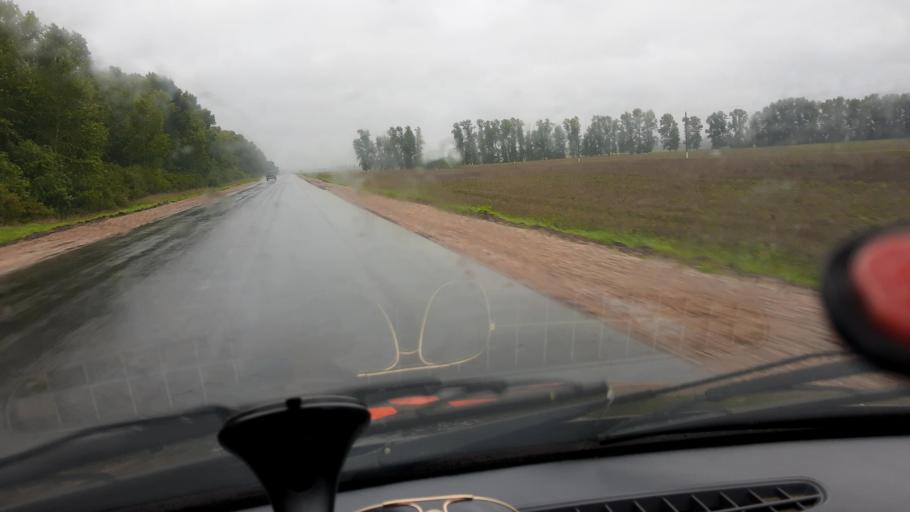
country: RU
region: Bashkortostan
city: Karmaskaly
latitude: 53.9625
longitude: 56.3986
